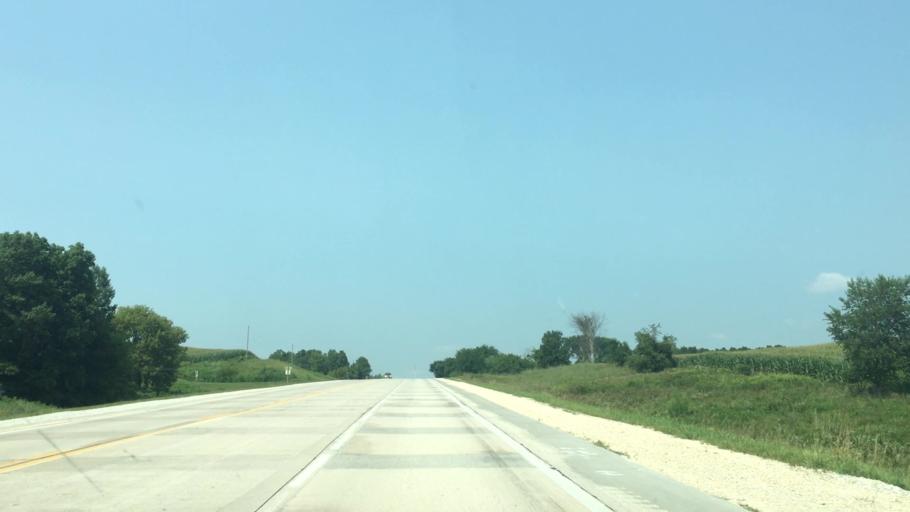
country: US
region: Iowa
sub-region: Winneshiek County
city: Decorah
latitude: 43.3281
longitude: -91.8131
